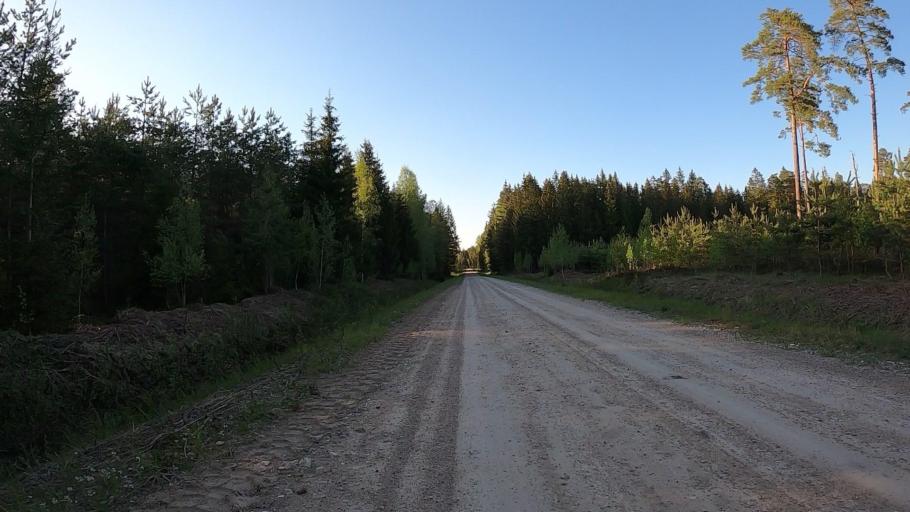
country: LV
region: Kekava
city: Kekava
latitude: 56.7515
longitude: 24.2310
